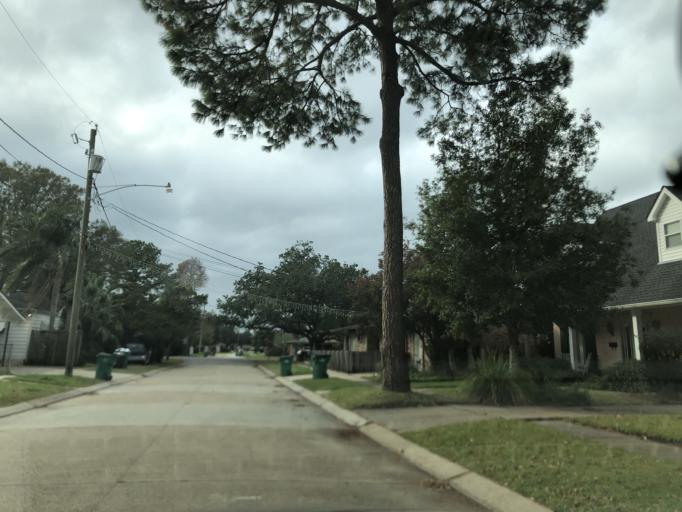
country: US
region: Louisiana
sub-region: Jefferson Parish
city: Metairie
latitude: 29.9846
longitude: -90.1593
